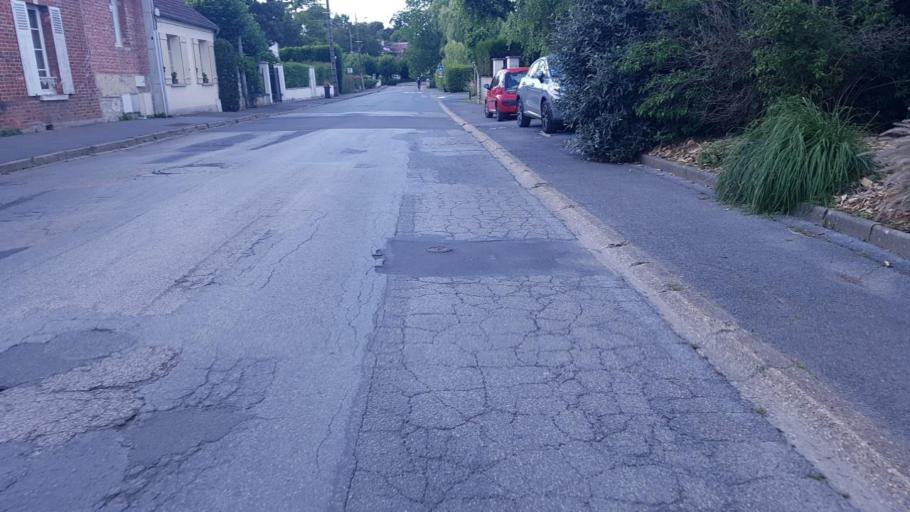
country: FR
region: Picardie
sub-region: Departement de l'Oise
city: Senlis
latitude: 49.1999
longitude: 2.5923
